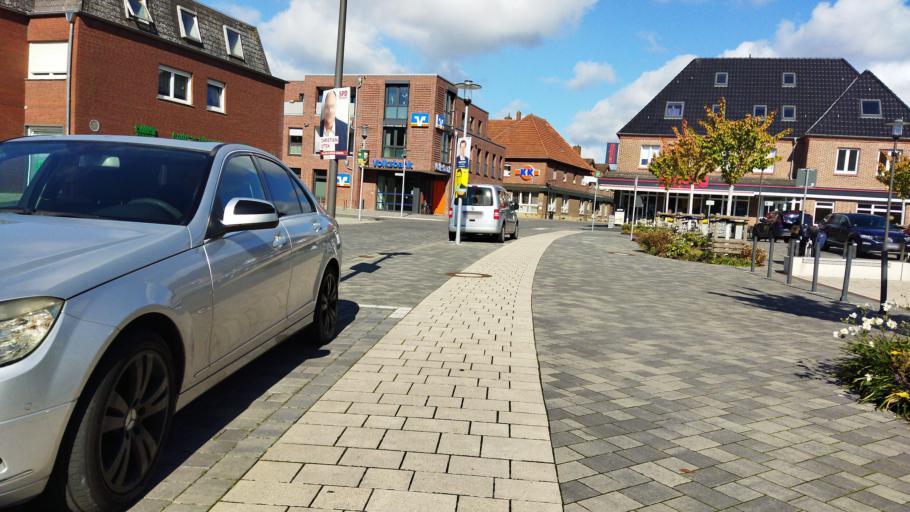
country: DE
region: Lower Saxony
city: Salzbergen
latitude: 52.3231
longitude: 7.3474
